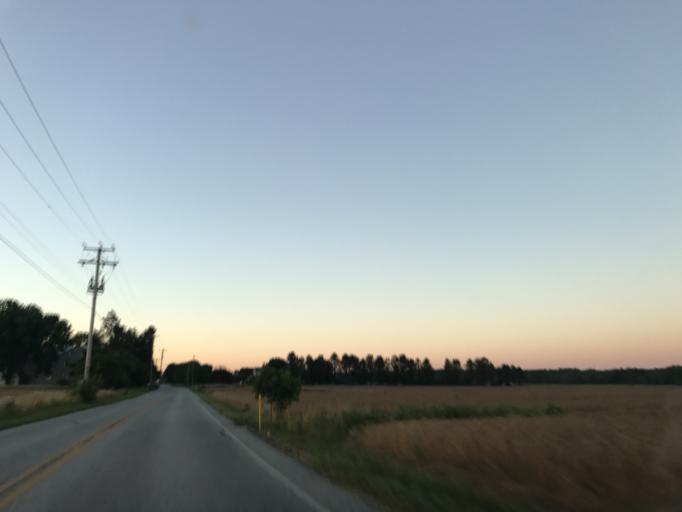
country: US
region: Pennsylvania
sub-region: Adams County
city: McSherrystown
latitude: 39.7893
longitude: -77.0388
